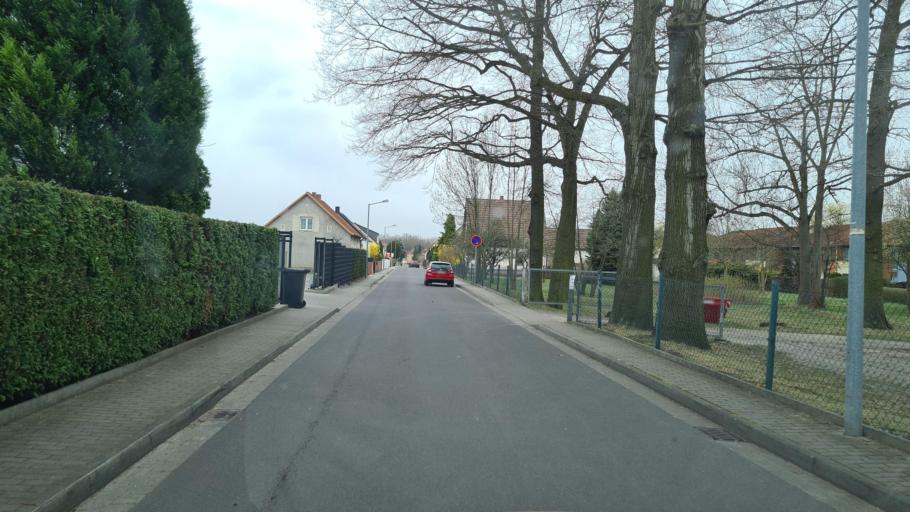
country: DE
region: Brandenburg
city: Lauchhammer
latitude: 51.4970
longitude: 13.7847
